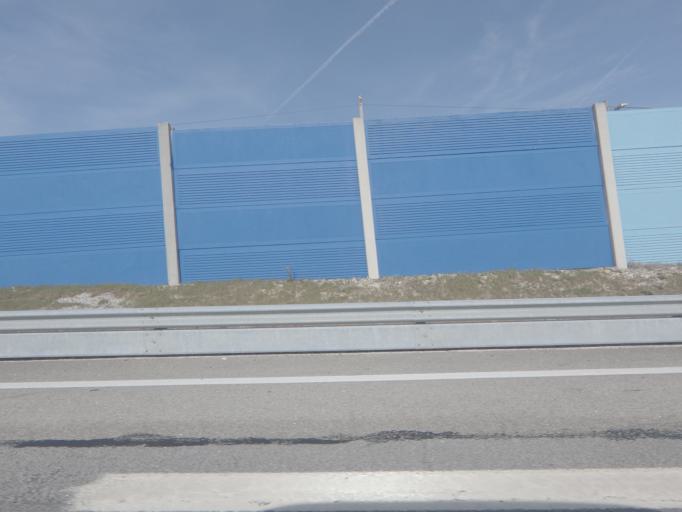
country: PT
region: Viseu
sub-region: Oliveira de Frades
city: Oliveira de Frades
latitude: 40.6880
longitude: -8.2359
